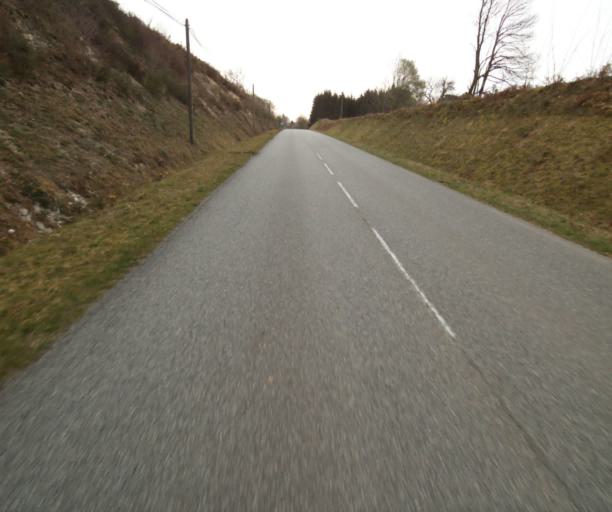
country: FR
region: Limousin
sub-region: Departement de la Correze
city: Correze
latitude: 45.4316
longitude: 1.8255
